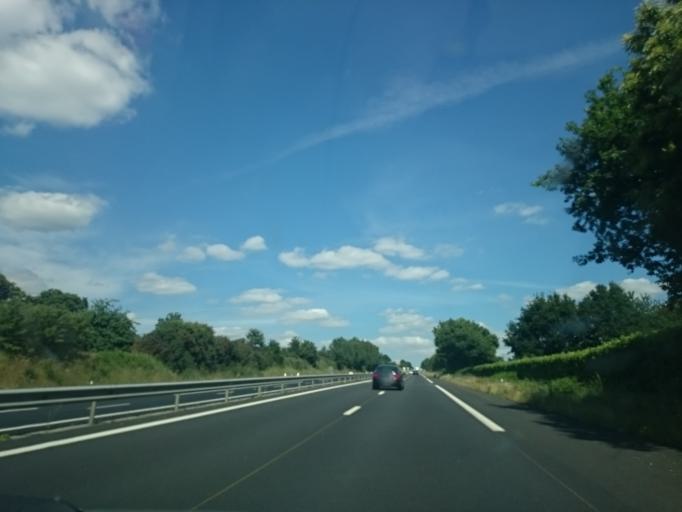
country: FR
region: Brittany
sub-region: Departement des Cotes-d'Armor
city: Plemet
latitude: 48.1687
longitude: -2.6337
